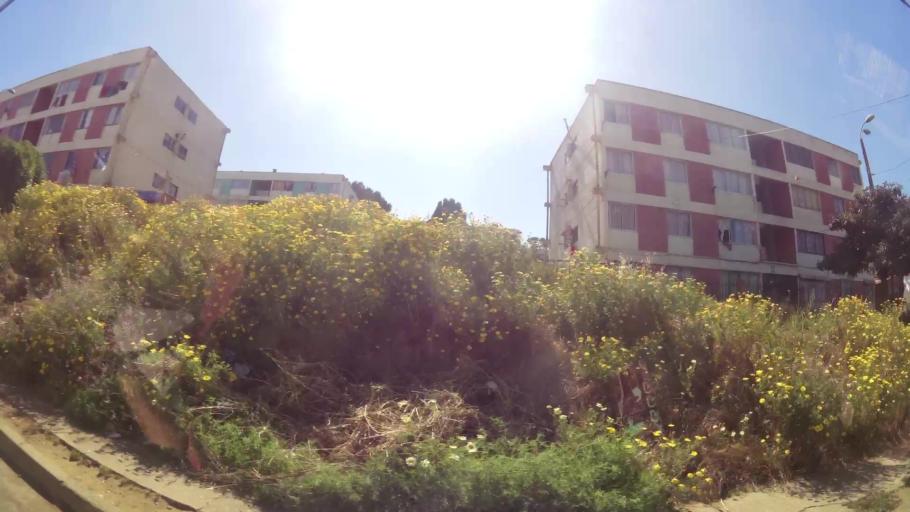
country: CL
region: Valparaiso
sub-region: Provincia de Valparaiso
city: Valparaiso
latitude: -33.0499
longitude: -71.6519
